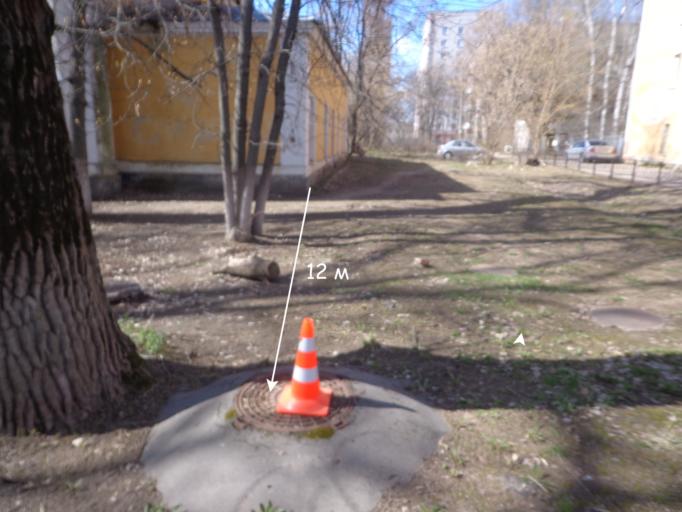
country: RU
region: Voronezj
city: Voronezh
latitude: 51.7155
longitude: 39.2225
